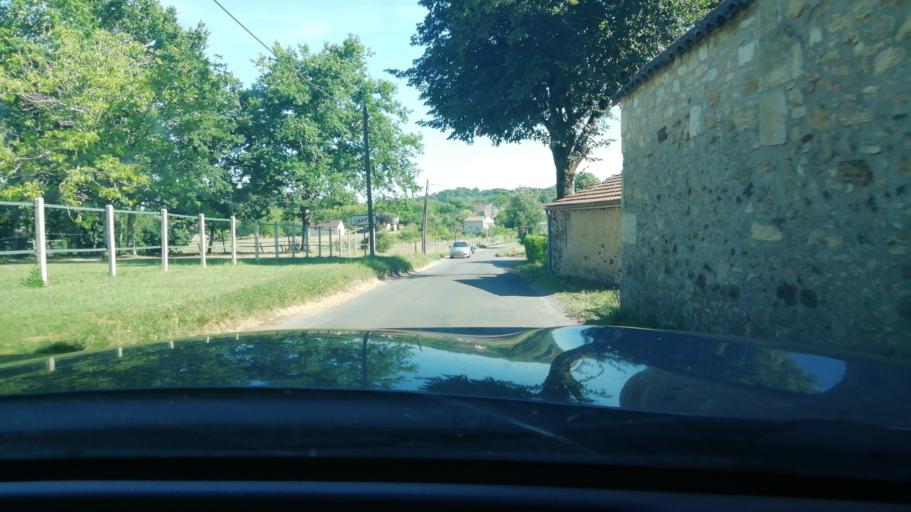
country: FR
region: Aquitaine
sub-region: Departement de la Dordogne
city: Sarlat-la-Caneda
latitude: 44.8654
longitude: 1.2297
